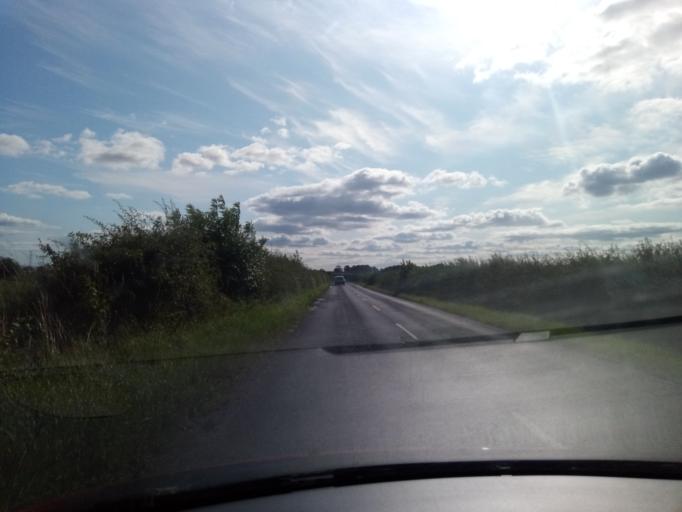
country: GB
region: Scotland
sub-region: The Scottish Borders
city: Allanton
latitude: 55.7490
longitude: -2.1579
